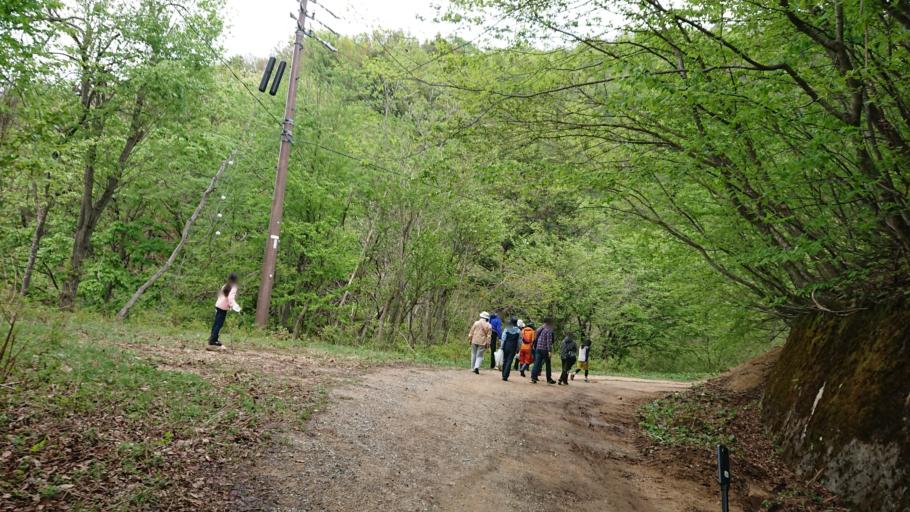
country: JP
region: Nagano
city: Omachi
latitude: 36.5050
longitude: 137.7987
